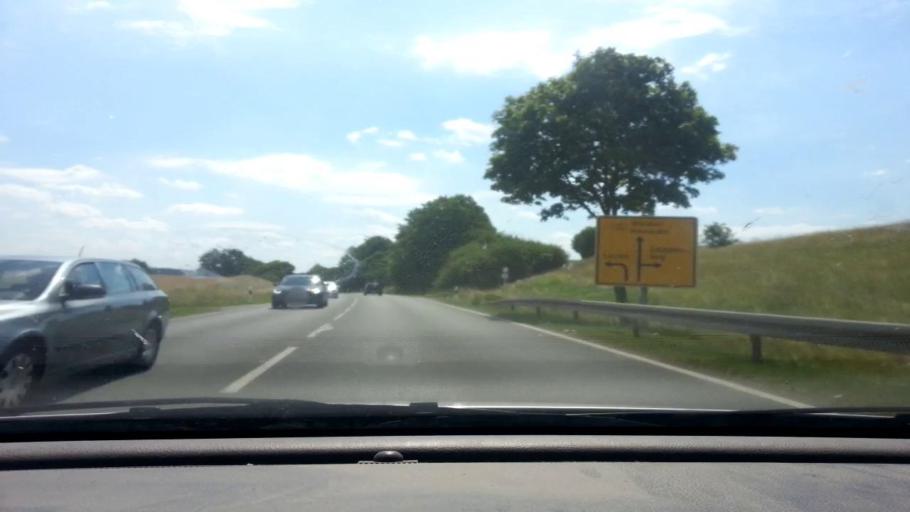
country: DE
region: Bavaria
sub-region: Upper Franconia
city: Emtmannsberg
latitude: 49.9120
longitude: 11.6571
